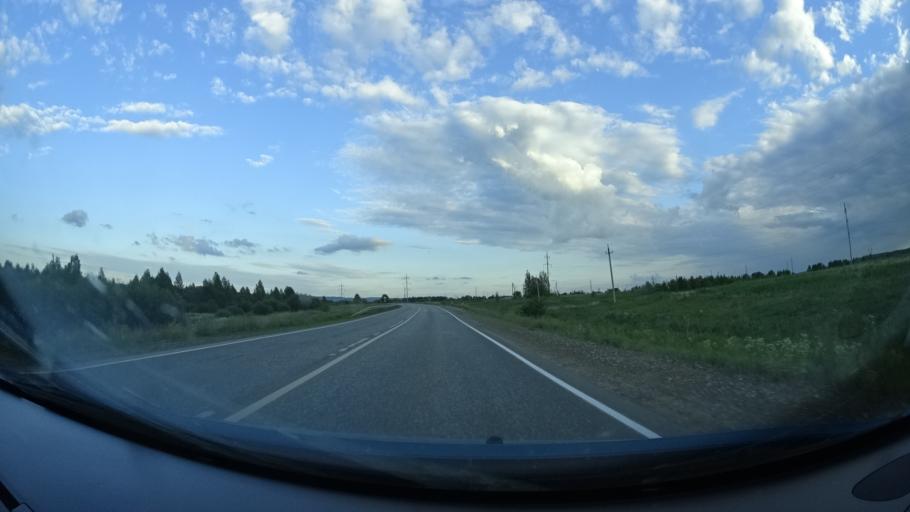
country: RU
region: Perm
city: Barda
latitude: 56.9512
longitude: 55.5835
